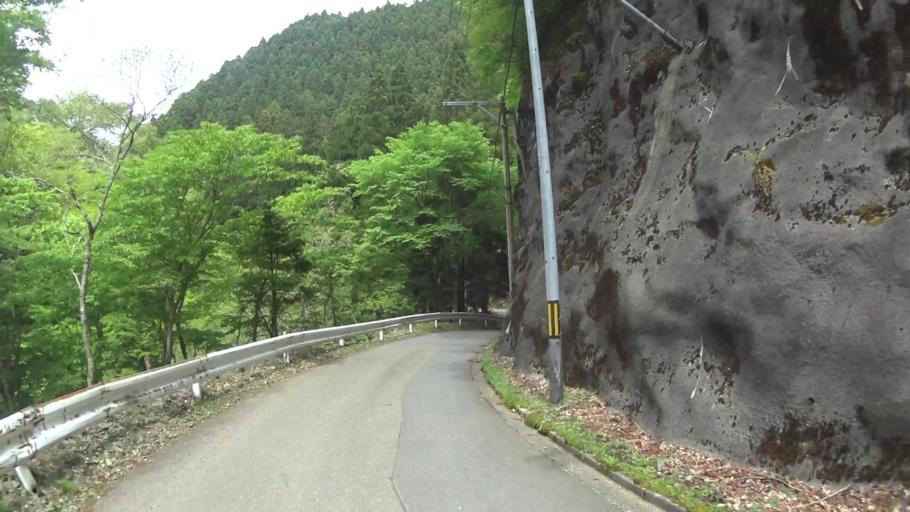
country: JP
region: Kyoto
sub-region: Kyoto-shi
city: Kamigyo-ku
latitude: 35.1710
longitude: 135.7423
